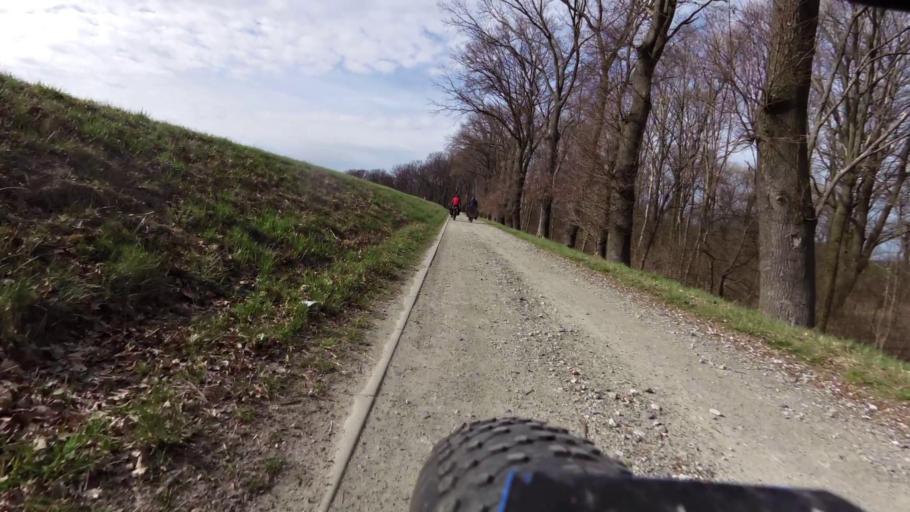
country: PL
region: Lubusz
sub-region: Powiat slubicki
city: Gorzyca
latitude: 52.5043
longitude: 14.6321
